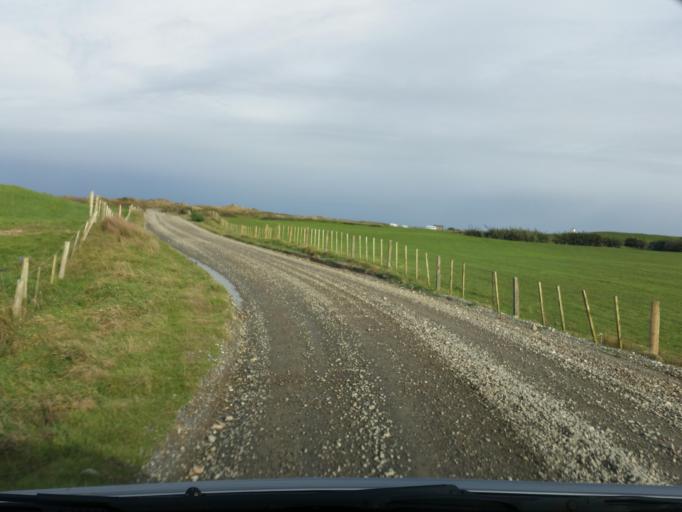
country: NZ
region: Southland
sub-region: Invercargill City
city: Bluff
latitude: -46.6554
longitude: 168.8560
